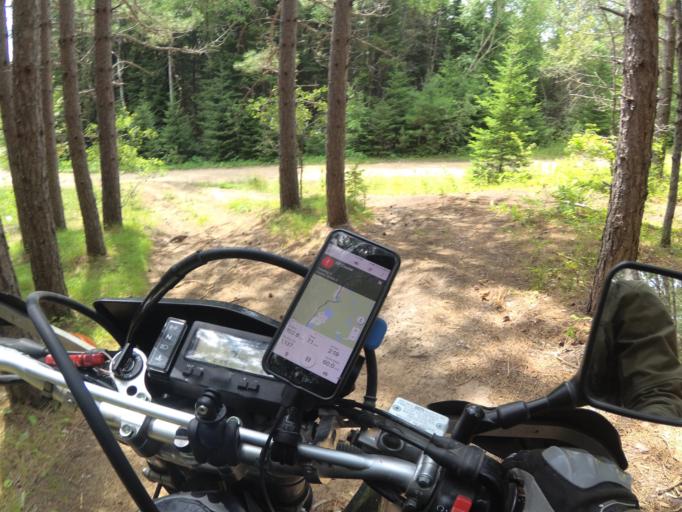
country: CA
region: Ontario
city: Bancroft
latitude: 45.0217
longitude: -77.2643
